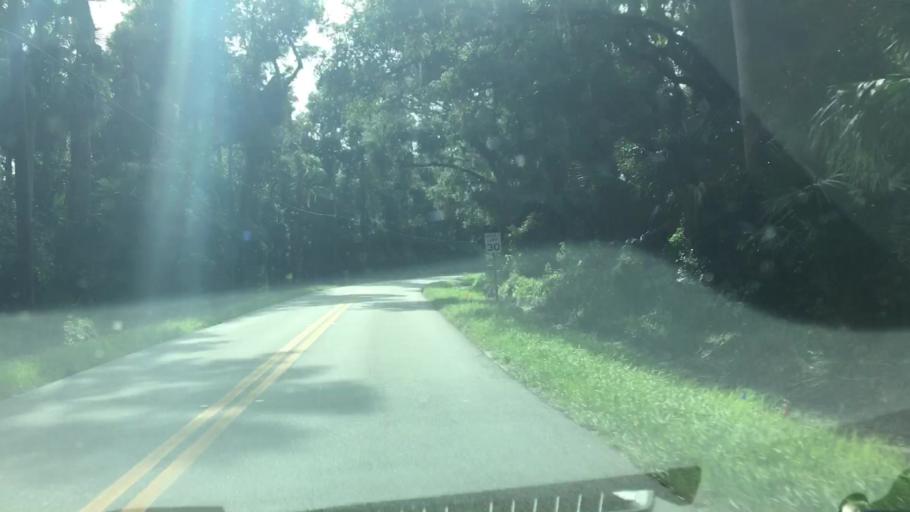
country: US
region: Florida
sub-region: Volusia County
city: Deltona
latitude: 28.8567
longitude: -81.2253
